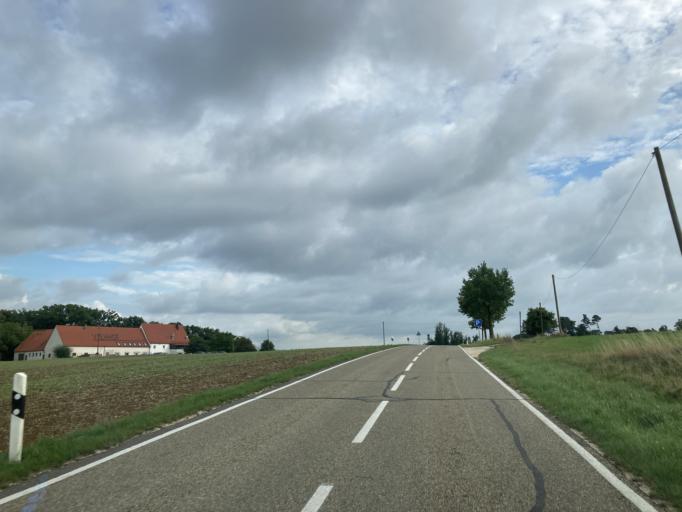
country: DE
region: Bavaria
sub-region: Swabia
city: Bachhagel
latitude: 48.6043
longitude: 10.3088
